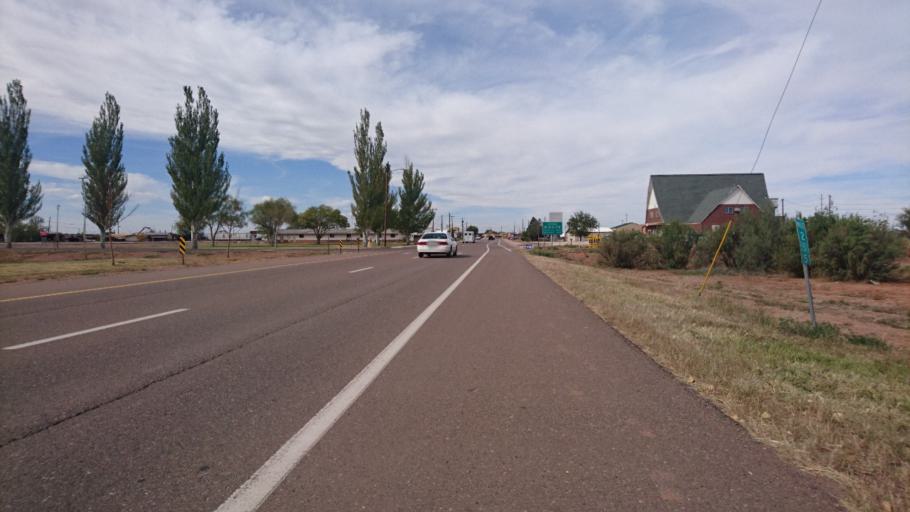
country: US
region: Arizona
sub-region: Navajo County
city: Winslow
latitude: 35.0160
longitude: -110.6801
